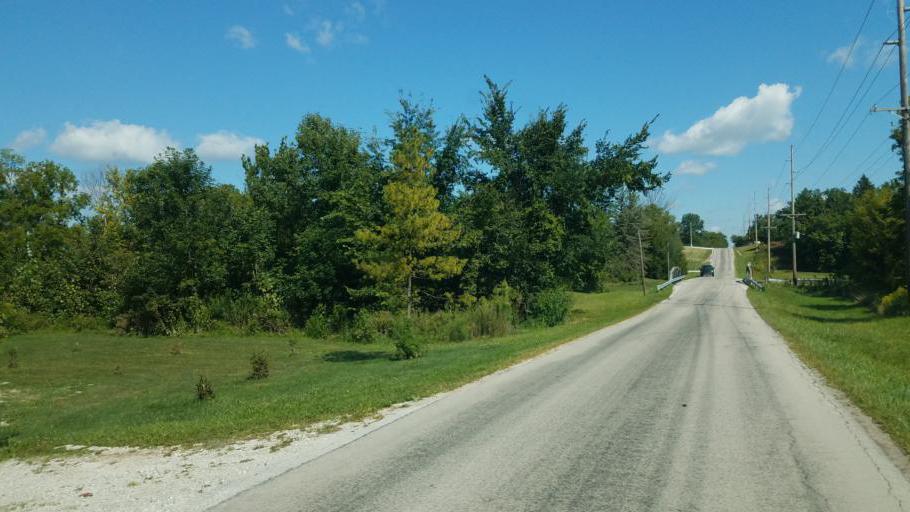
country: US
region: Ohio
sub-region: Wyandot County
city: Carey
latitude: 40.9487
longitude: -83.3193
